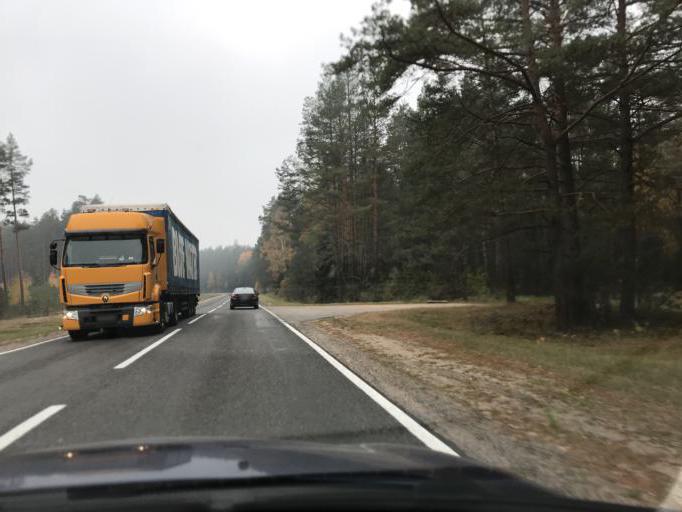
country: LT
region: Alytaus apskritis
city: Druskininkai
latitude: 53.8729
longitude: 23.8968
